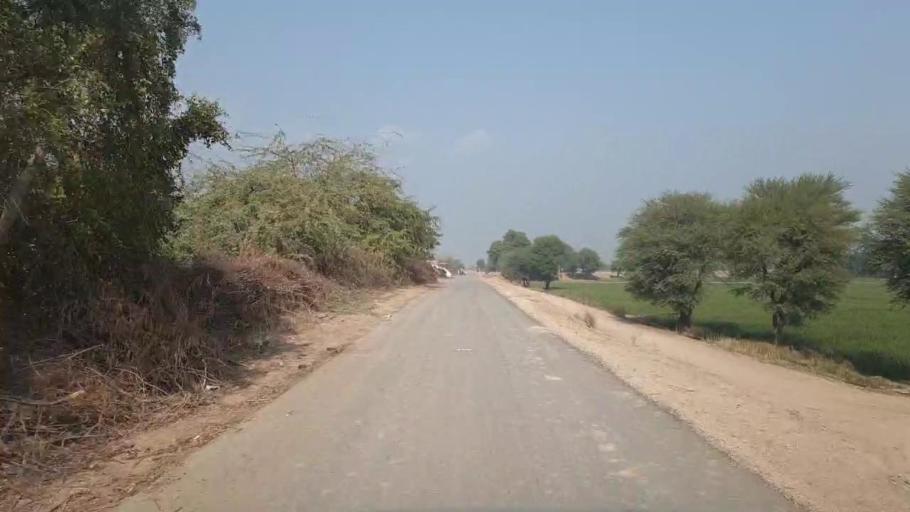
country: PK
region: Sindh
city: Hala
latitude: 25.7833
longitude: 68.3997
